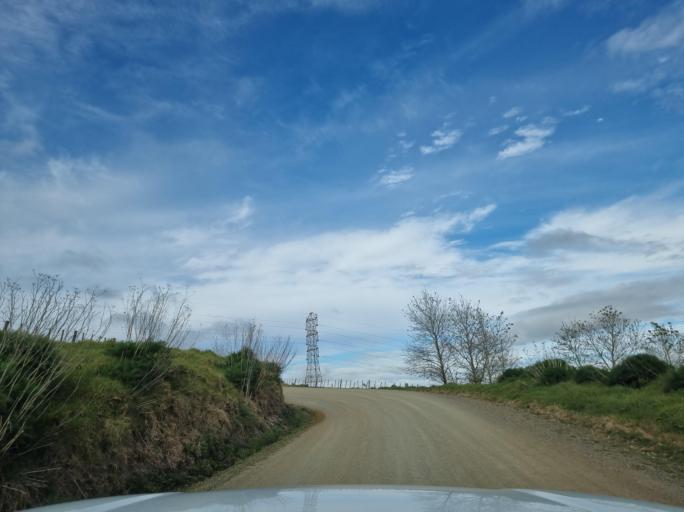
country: NZ
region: Northland
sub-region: Whangarei
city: Ruakaka
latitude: -36.0893
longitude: 174.3668
